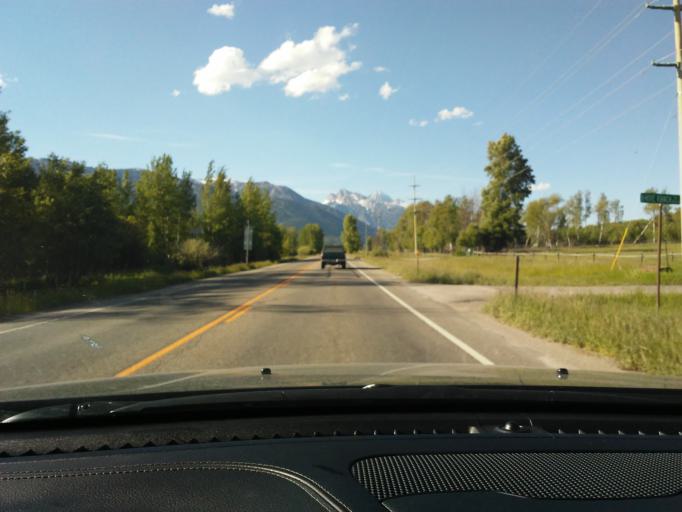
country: US
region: Wyoming
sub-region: Teton County
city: Moose Wilson Road
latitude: 43.5490
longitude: -110.8222
